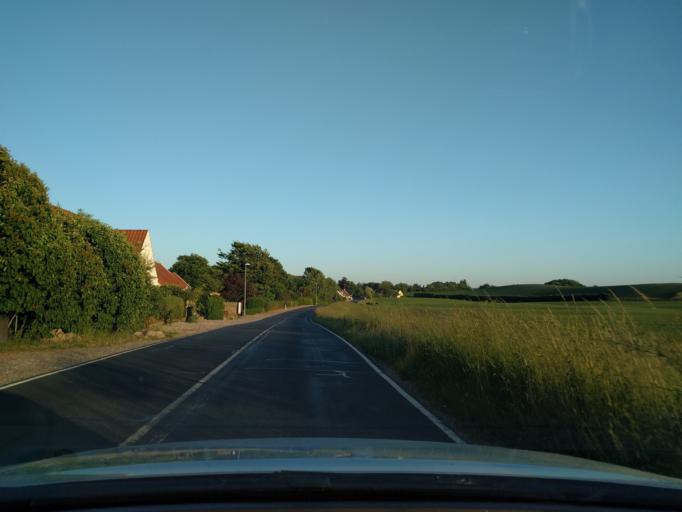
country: DK
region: South Denmark
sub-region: Kerteminde Kommune
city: Kerteminde
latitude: 55.5226
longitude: 10.6541
